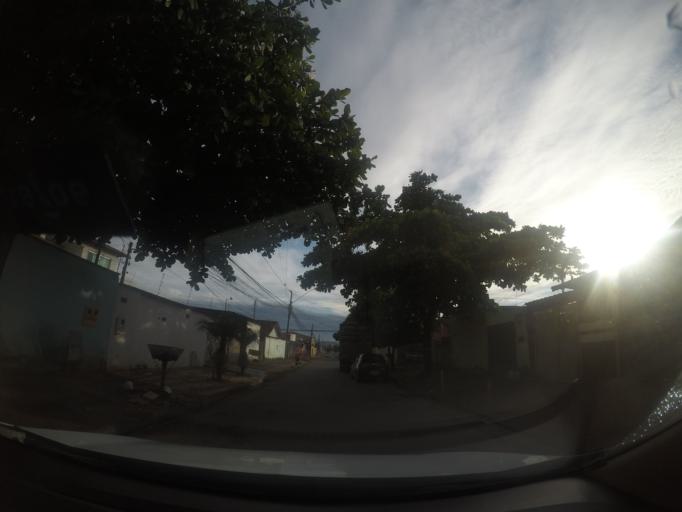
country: BR
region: Goias
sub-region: Goiania
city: Goiania
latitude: -16.6454
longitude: -49.3226
